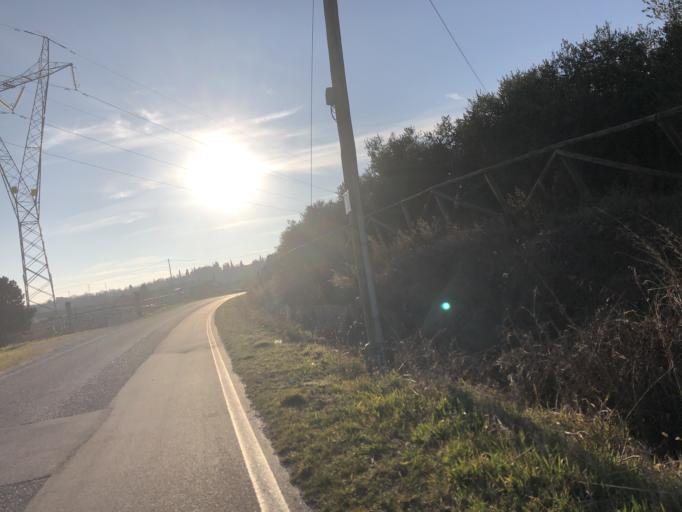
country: IT
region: Veneto
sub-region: Provincia di Verona
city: Bussolengo
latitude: 45.4715
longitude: 10.8227
